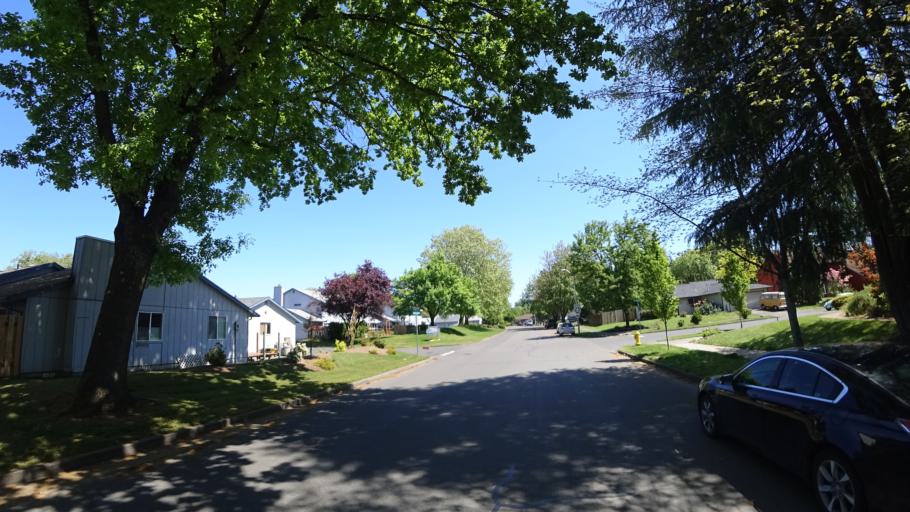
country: US
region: Oregon
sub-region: Washington County
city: Hillsboro
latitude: 45.5012
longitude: -122.9646
